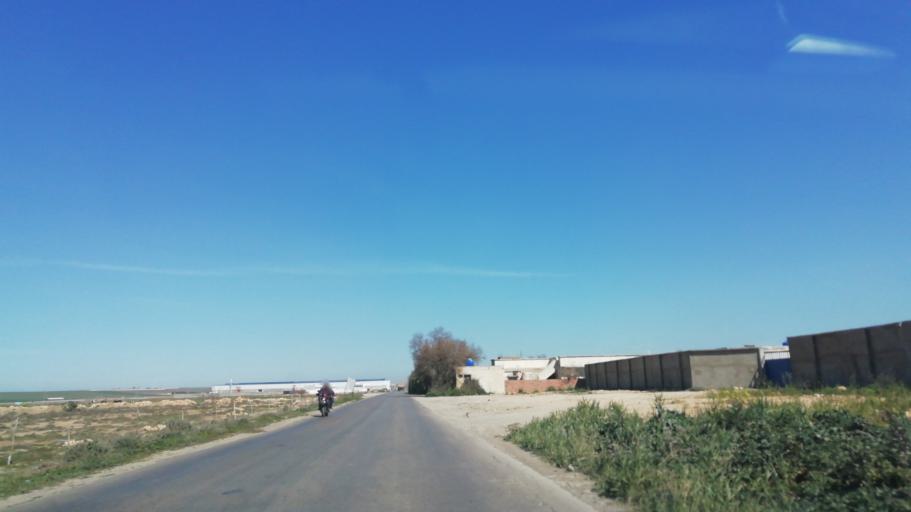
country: DZ
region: Oran
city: Es Senia
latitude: 35.5023
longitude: -0.5945
